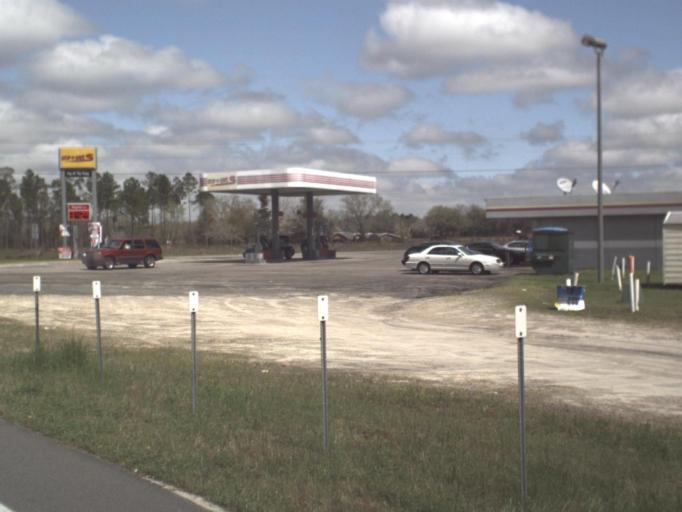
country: US
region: Florida
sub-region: Wakulla County
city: Crawfordville
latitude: 30.2623
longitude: -84.3621
